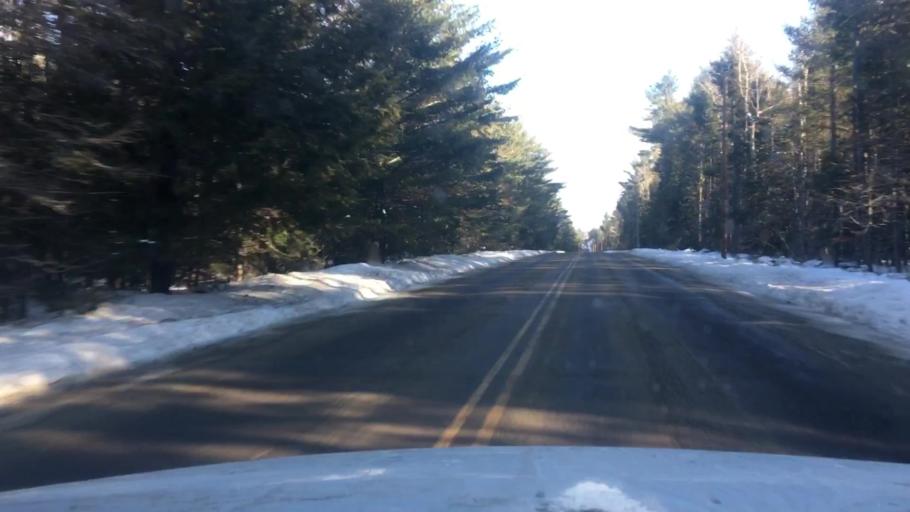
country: US
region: Maine
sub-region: Hancock County
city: Ellsworth
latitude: 44.6648
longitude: -68.3558
